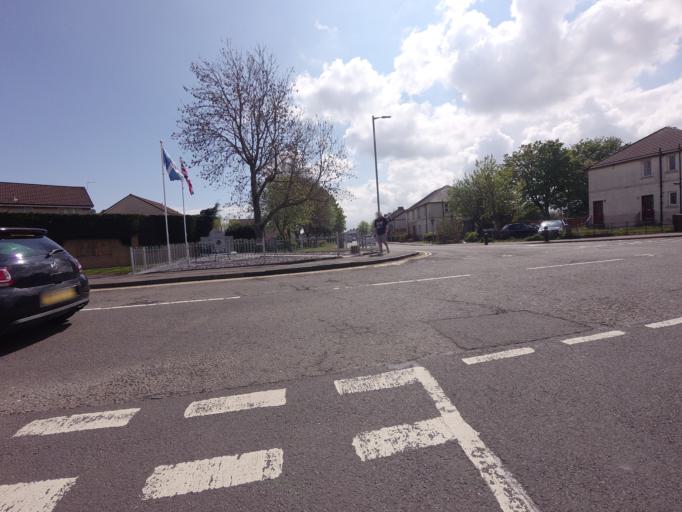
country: GB
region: Scotland
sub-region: Falkirk
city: Falkirk
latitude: 56.0287
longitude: -3.7833
